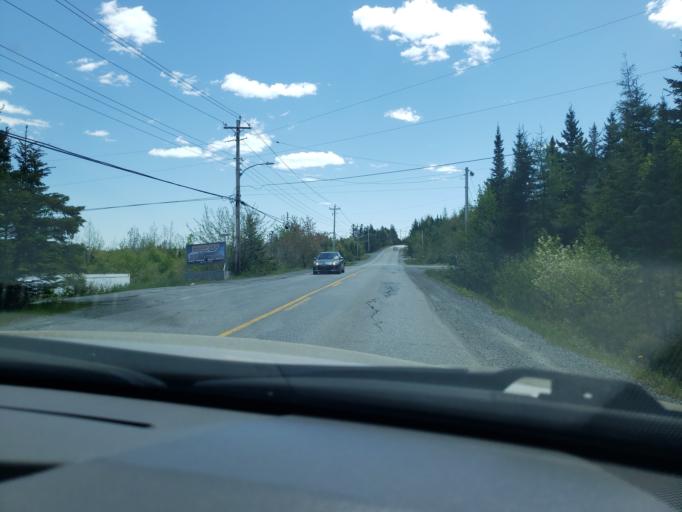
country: CA
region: Nova Scotia
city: Cole Harbour
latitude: 44.7294
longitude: -63.3069
